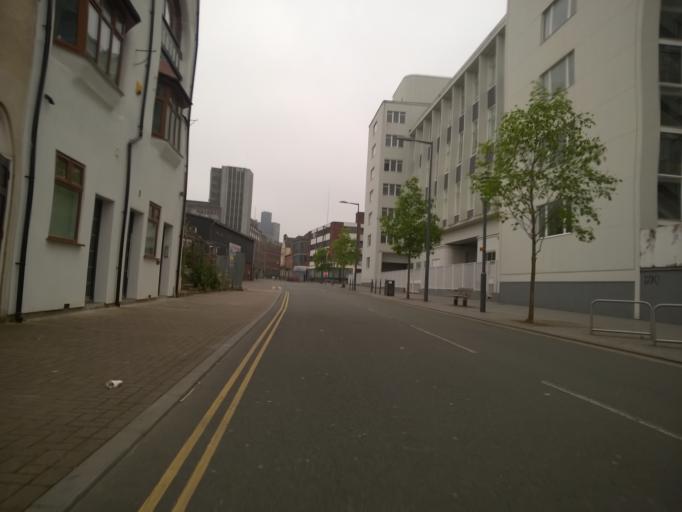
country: GB
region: England
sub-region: City of Leicester
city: Leicester
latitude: 52.6385
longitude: -1.1274
